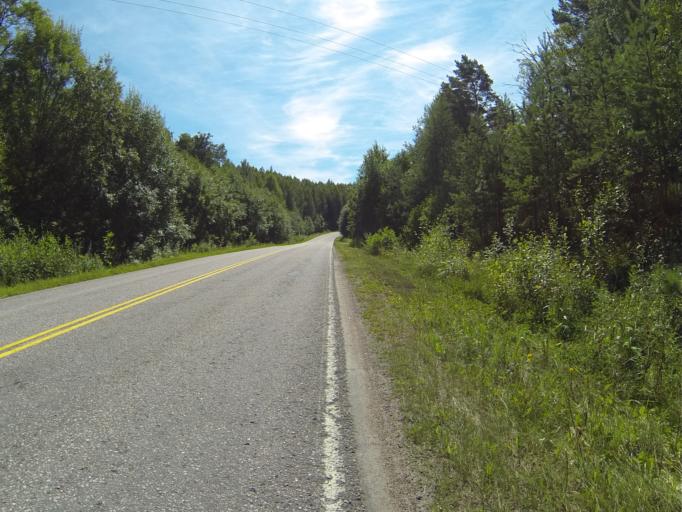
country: FI
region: Varsinais-Suomi
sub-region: Salo
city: Halikko
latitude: 60.2736
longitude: 22.9833
